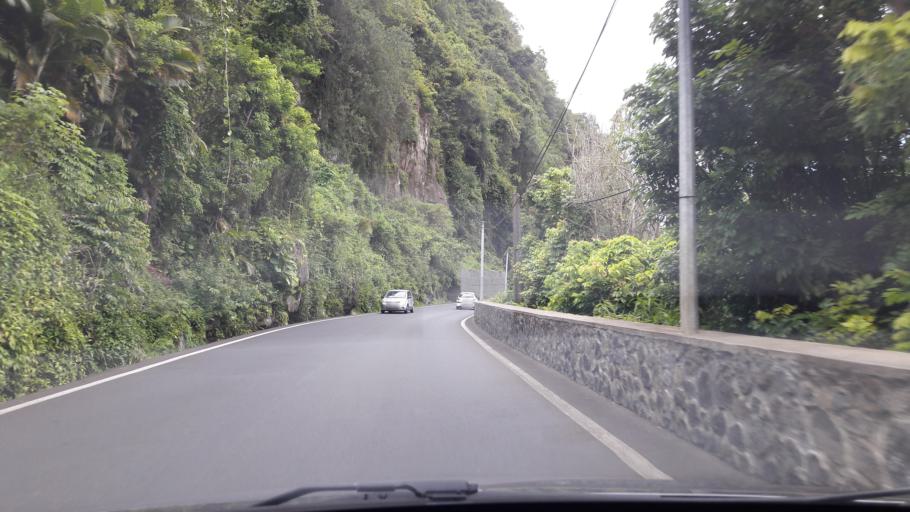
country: RE
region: Reunion
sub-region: Reunion
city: Saint-Andre
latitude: -20.9874
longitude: 55.6204
